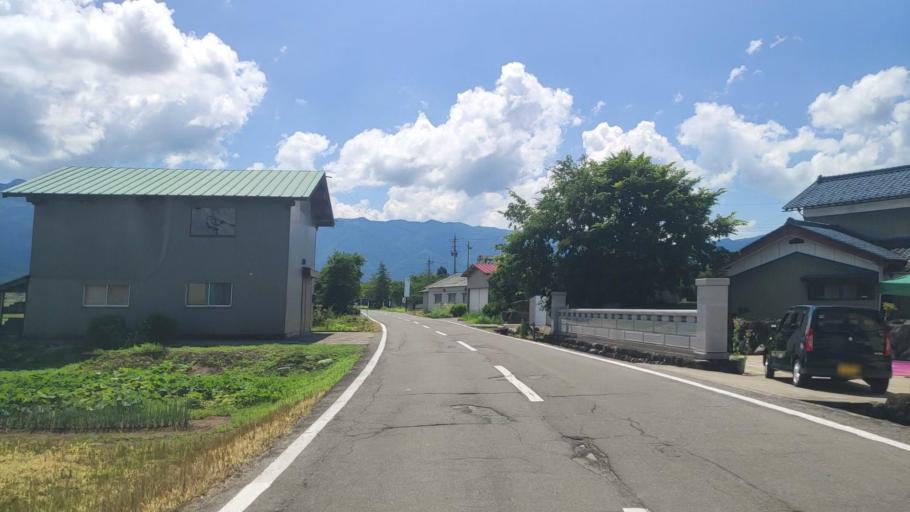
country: JP
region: Fukui
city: Ono
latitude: 35.9710
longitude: 136.5255
